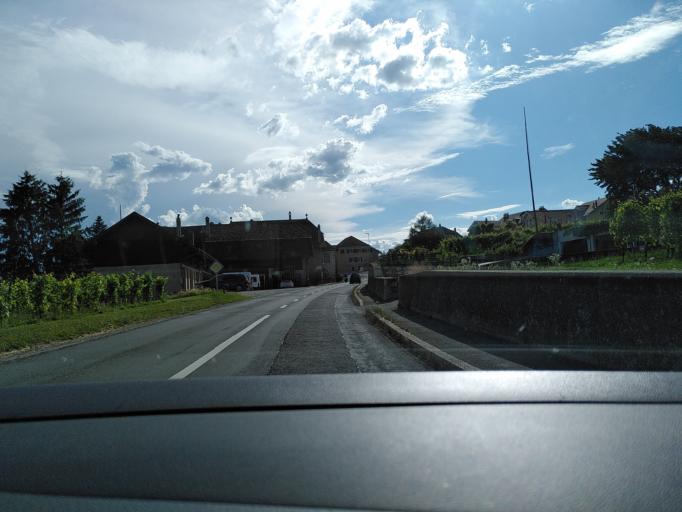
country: CH
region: Vaud
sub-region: Nyon District
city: Rolle
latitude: 46.4698
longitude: 6.3424
